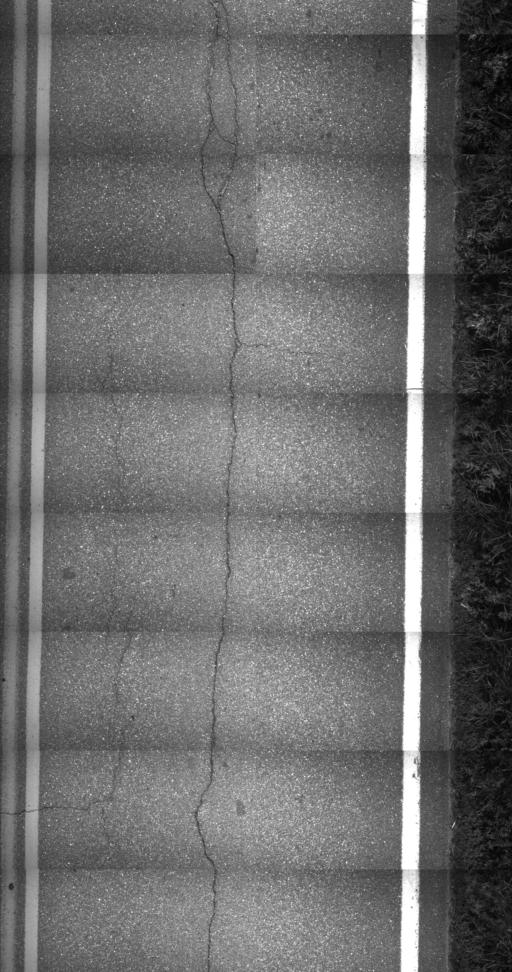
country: US
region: Vermont
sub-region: Orange County
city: Chelsea
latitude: 43.9434
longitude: -72.4614
